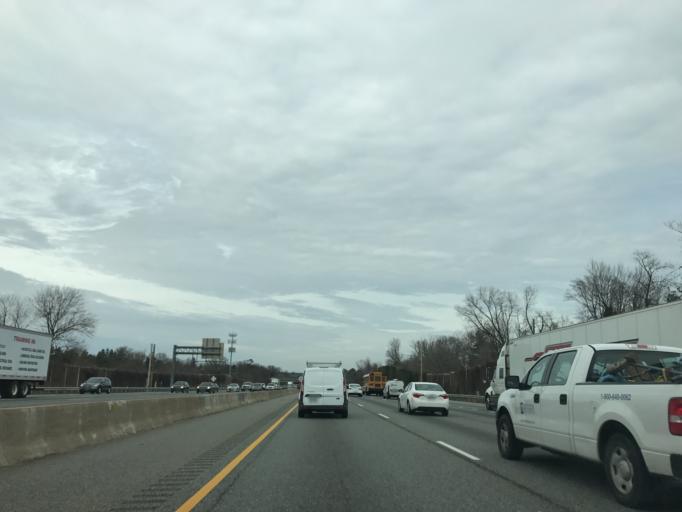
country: US
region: Maryland
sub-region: Baltimore County
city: Catonsville
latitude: 39.2931
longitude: -76.7423
